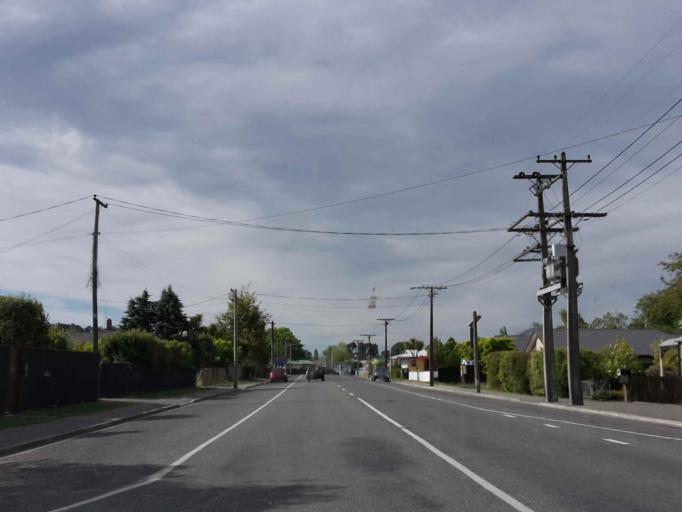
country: NZ
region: Canterbury
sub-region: Timaru District
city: Pleasant Point
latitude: -44.0959
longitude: 171.2400
